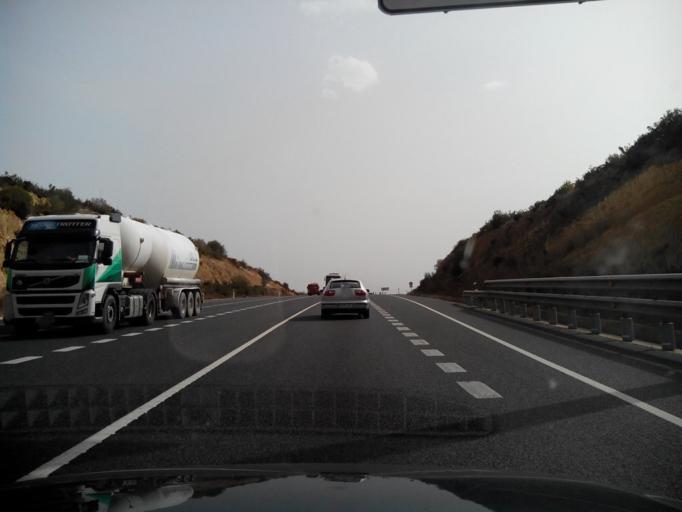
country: ES
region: Catalonia
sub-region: Provincia de Tarragona
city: Torredembarra
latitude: 41.1616
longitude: 1.4107
